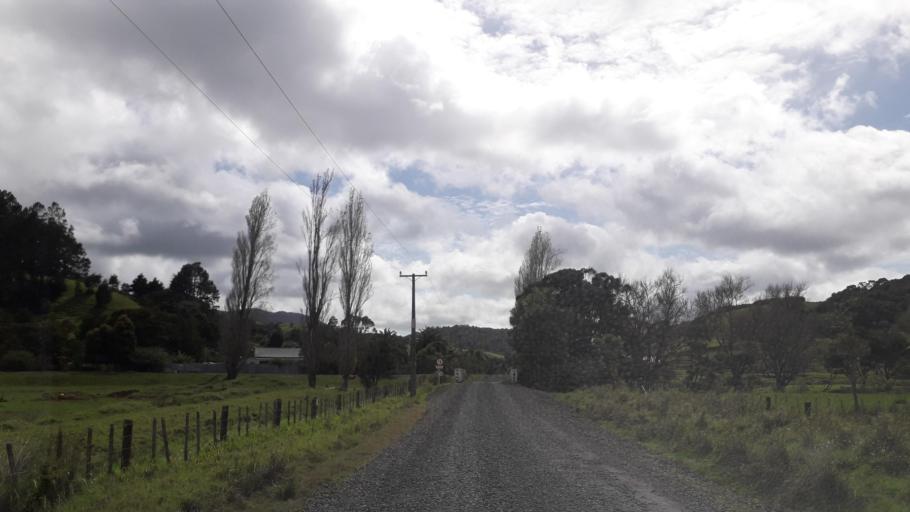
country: NZ
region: Northland
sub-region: Far North District
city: Ahipara
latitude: -35.2464
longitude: 173.2516
